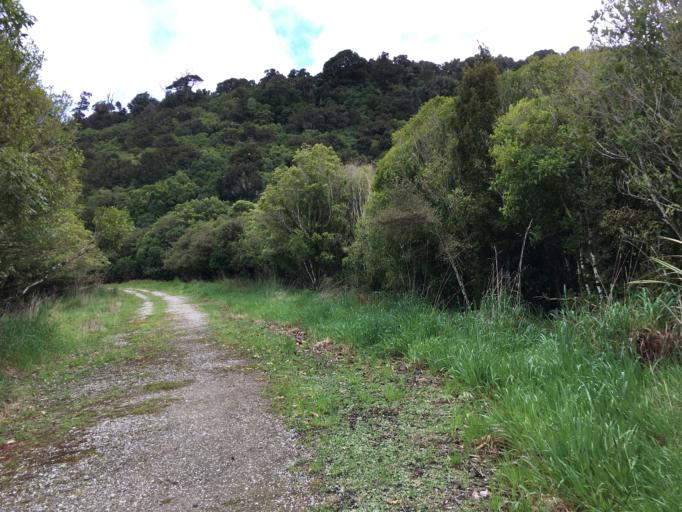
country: NZ
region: Otago
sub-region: Clutha District
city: Papatowai
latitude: -46.5039
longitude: 169.4846
